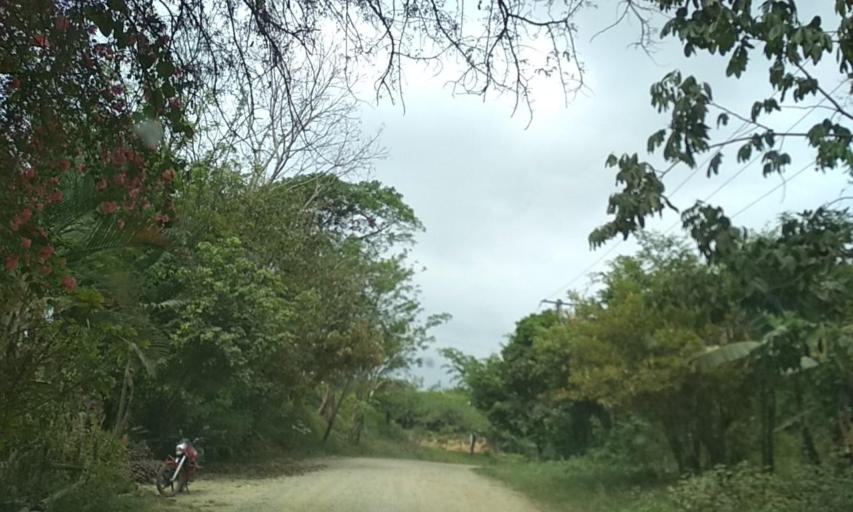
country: MX
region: Veracruz
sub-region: Uxpanapa
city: Poblado 10
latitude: 17.4572
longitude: -94.1005
